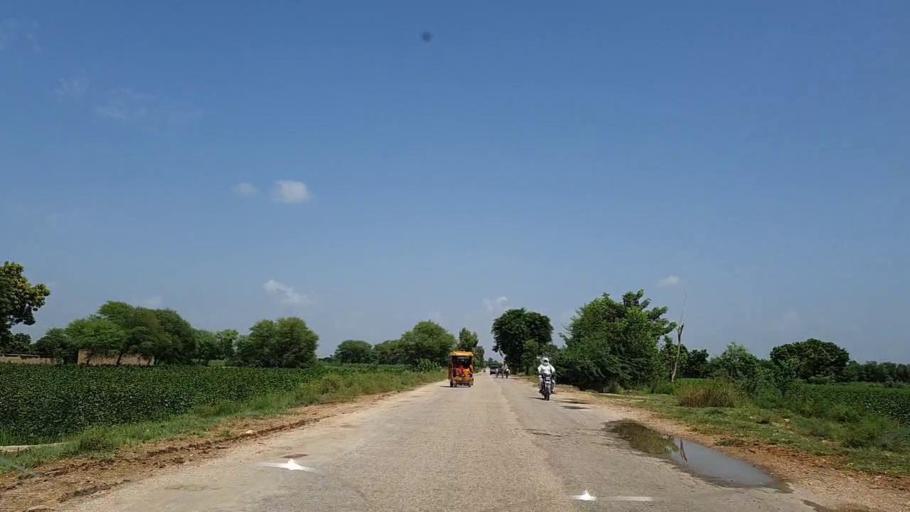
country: PK
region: Sindh
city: Pad Idan
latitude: 26.8020
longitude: 68.2217
